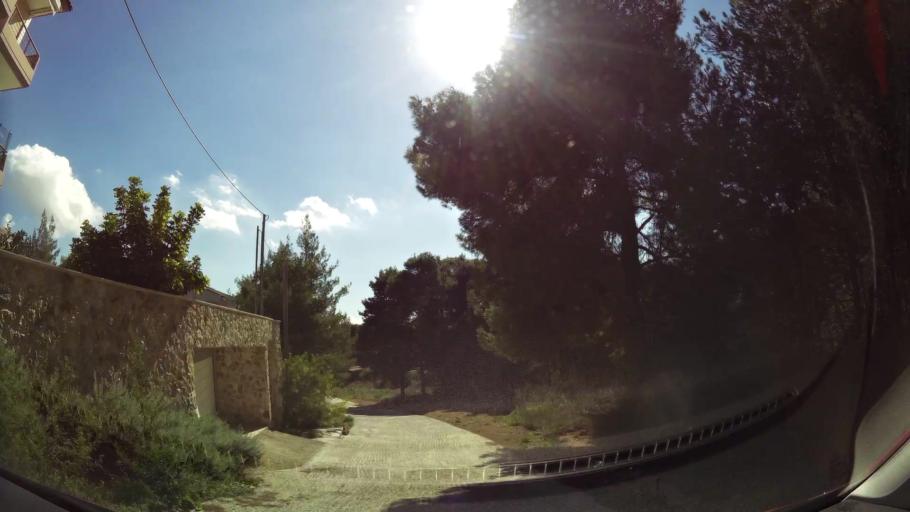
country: GR
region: Attica
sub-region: Nomarchia Anatolikis Attikis
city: Dioni
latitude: 38.0284
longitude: 23.9329
